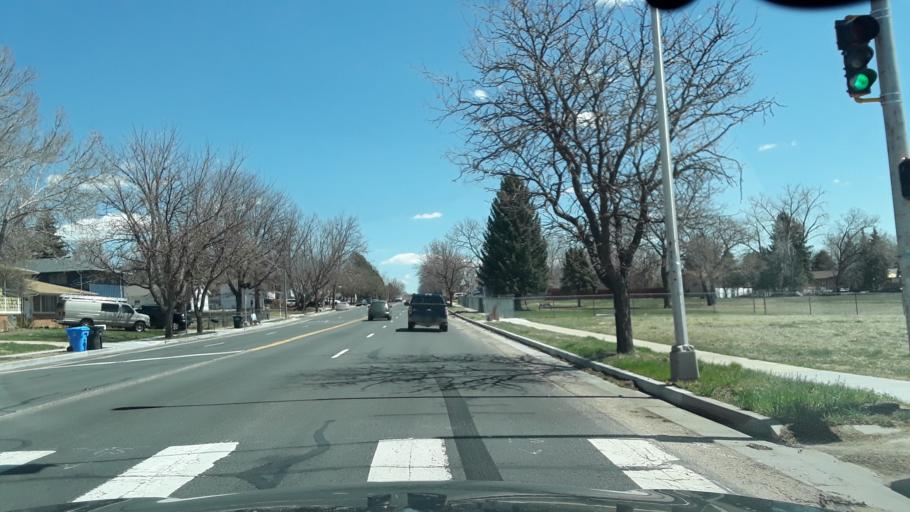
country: US
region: Colorado
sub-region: El Paso County
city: Cimarron Hills
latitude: 38.8543
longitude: -104.7462
